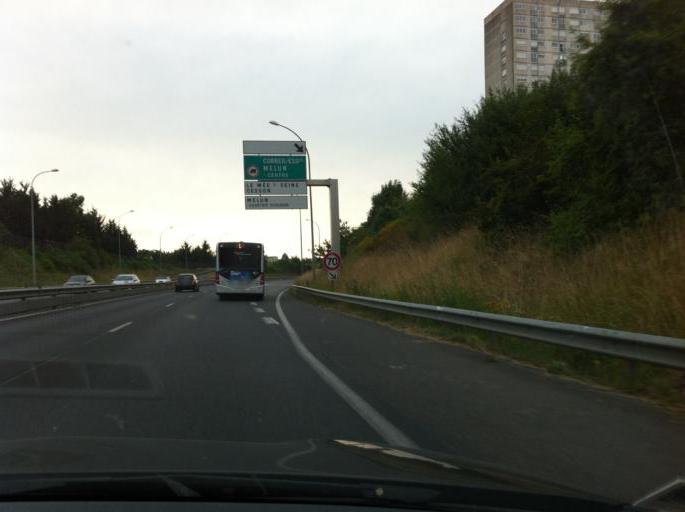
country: FR
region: Ile-de-France
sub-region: Departement de Seine-et-Marne
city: Le Mee-sur-Seine
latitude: 48.5457
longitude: 2.6436
